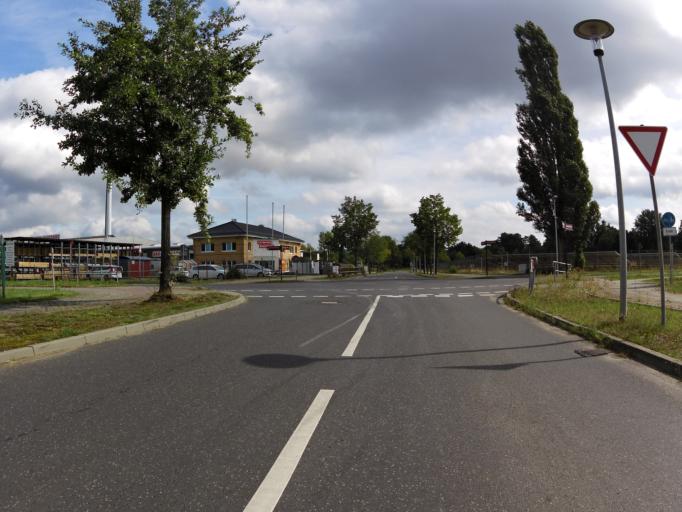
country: DE
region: Brandenburg
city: Storkow
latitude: 52.2684
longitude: 13.9420
